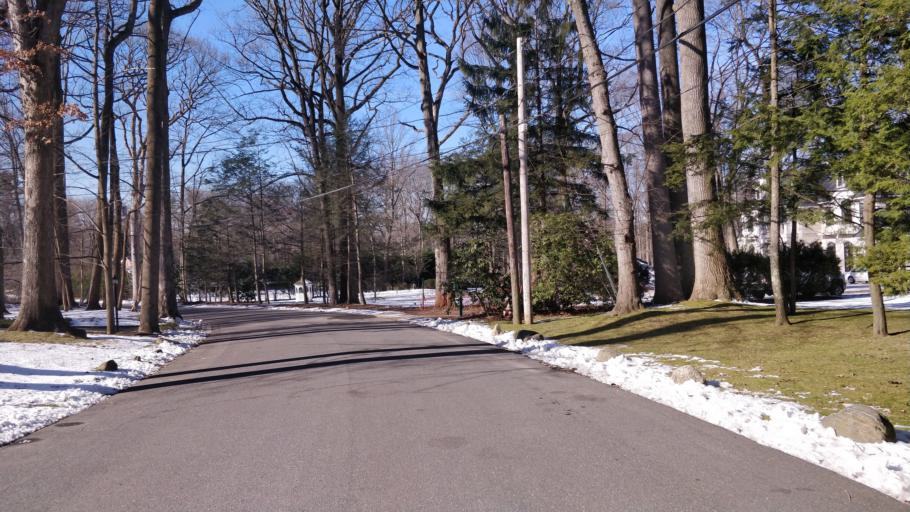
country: US
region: New York
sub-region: Nassau County
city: Old Brookville
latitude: 40.8499
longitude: -73.5971
